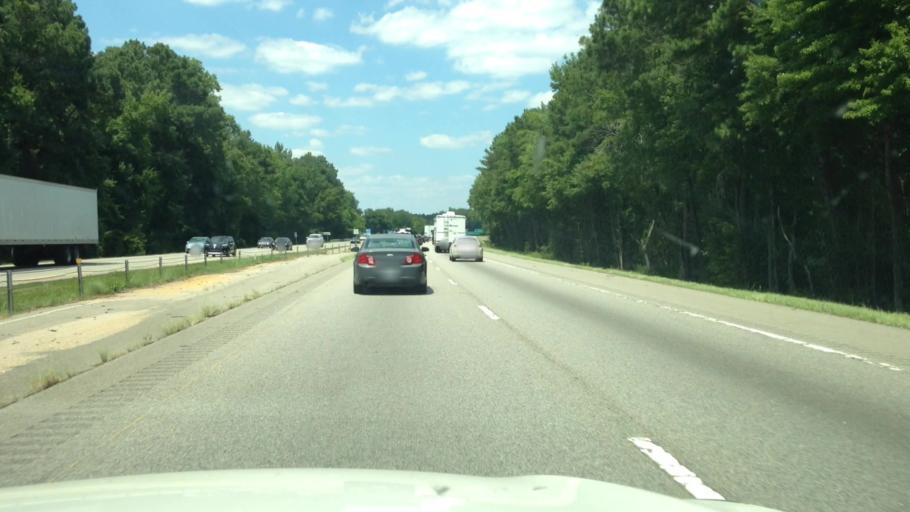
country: US
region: North Carolina
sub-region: Cumberland County
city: Hope Mills
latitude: 34.9102
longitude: -78.9553
